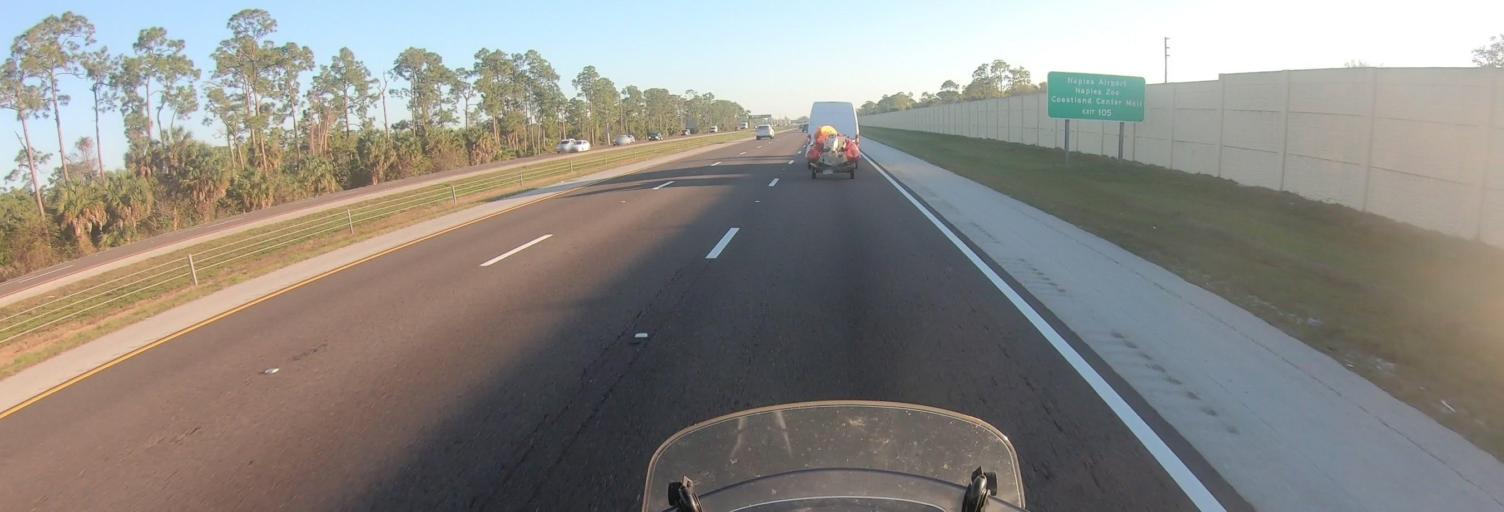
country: US
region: Florida
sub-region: Collier County
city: Golden Gate
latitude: 26.1921
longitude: -81.7351
